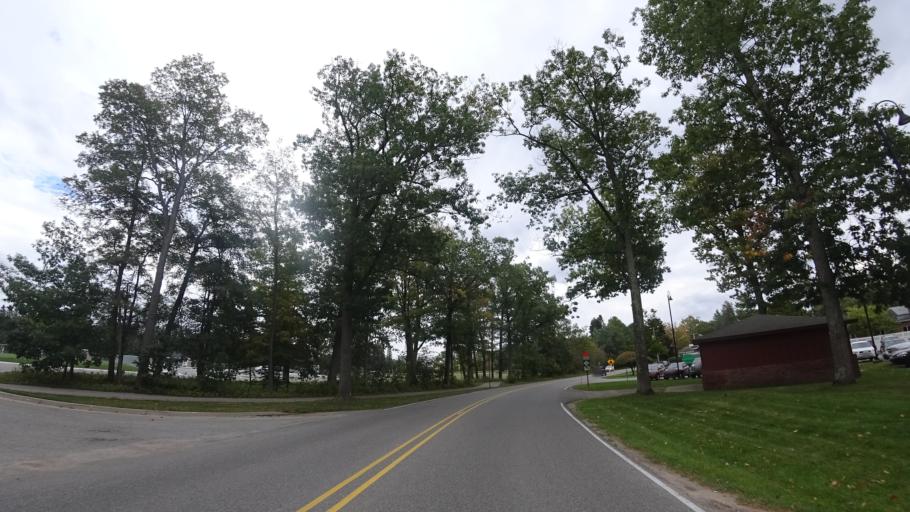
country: US
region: Michigan
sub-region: Emmet County
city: Harbor Springs
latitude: 45.4342
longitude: -84.9714
